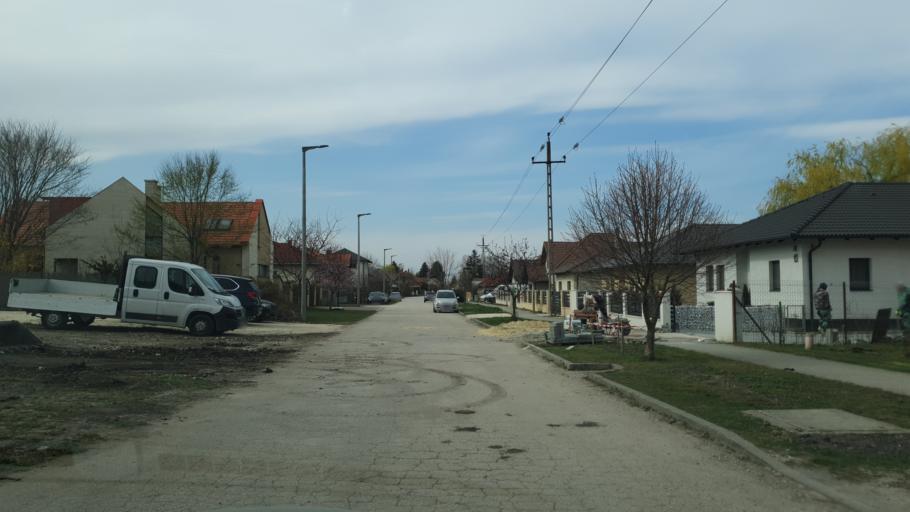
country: HU
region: Fejer
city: Etyek
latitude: 47.4409
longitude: 18.7531
